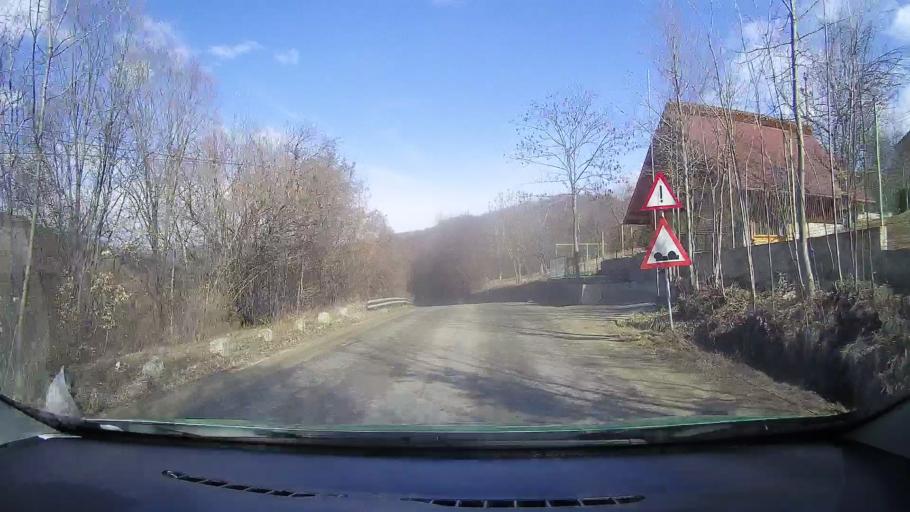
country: RO
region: Dambovita
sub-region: Comuna Runcu
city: Badeni
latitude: 45.1465
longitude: 25.4035
